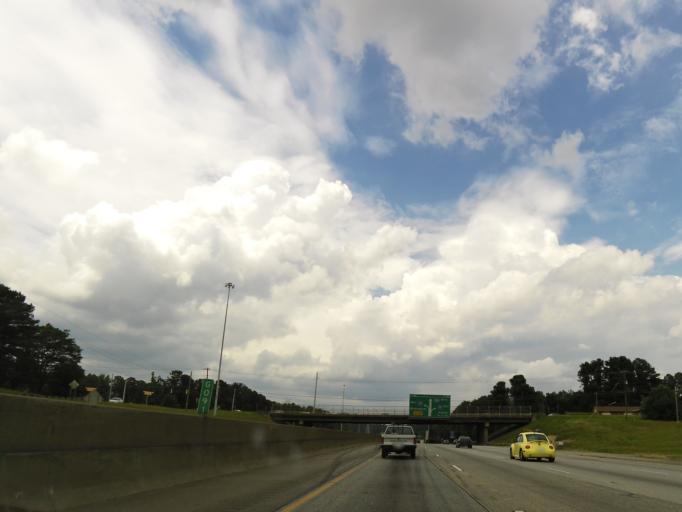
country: US
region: Georgia
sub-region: Fulton County
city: East Point
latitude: 33.7521
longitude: -84.4960
